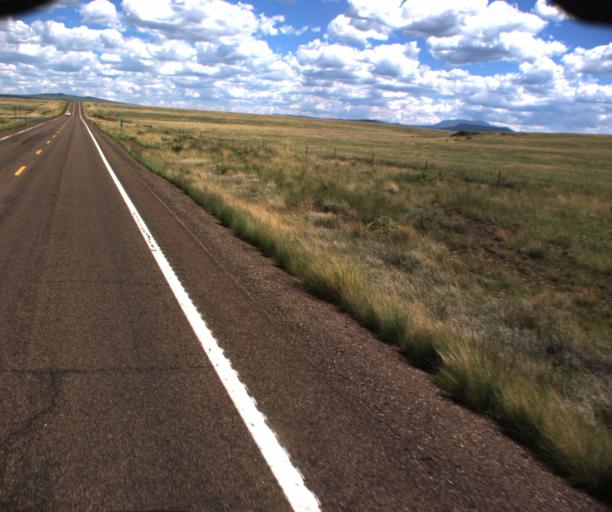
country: US
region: Arizona
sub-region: Apache County
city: Springerville
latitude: 34.1946
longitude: -109.3725
